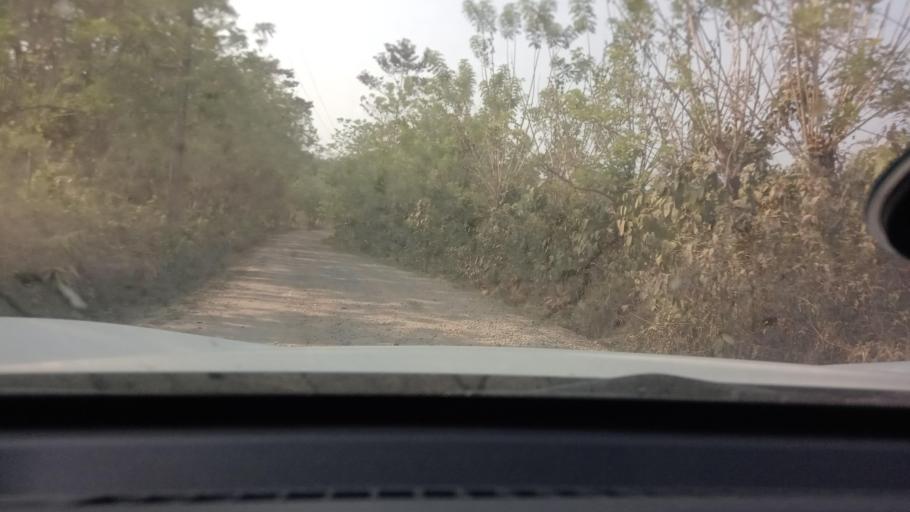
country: MX
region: Tabasco
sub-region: Huimanguillo
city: Francisco Rueda
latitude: 17.6539
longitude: -93.8770
